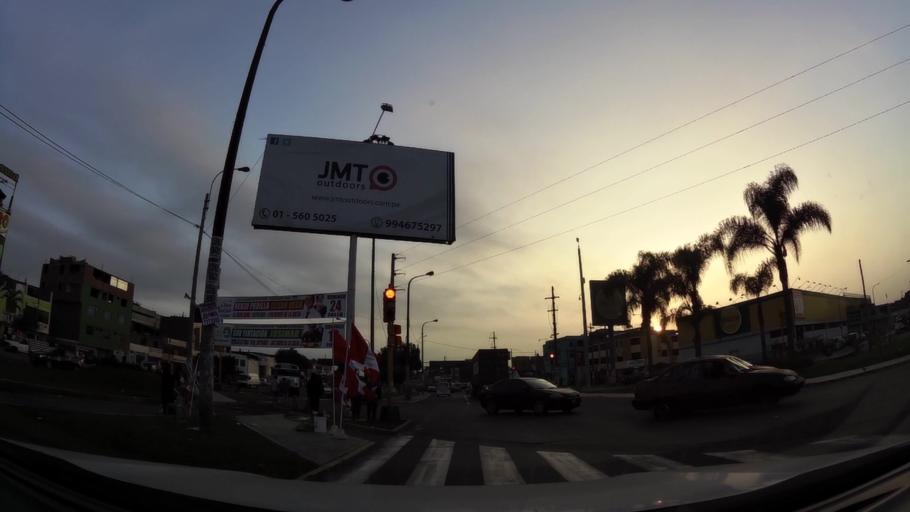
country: PE
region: Lima
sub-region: Lima
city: Independencia
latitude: -12.0116
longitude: -77.0897
